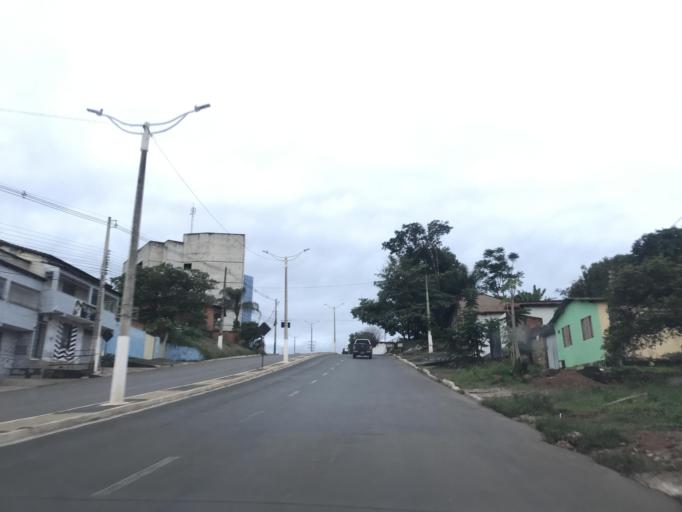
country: BR
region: Goias
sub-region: Luziania
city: Luziania
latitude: -16.2413
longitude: -47.9440
